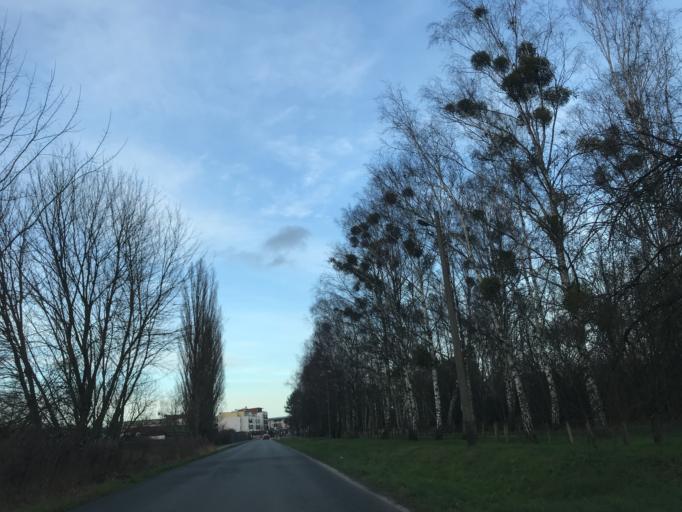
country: DE
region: Berlin
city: Staaken
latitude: 52.5548
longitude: 13.1338
